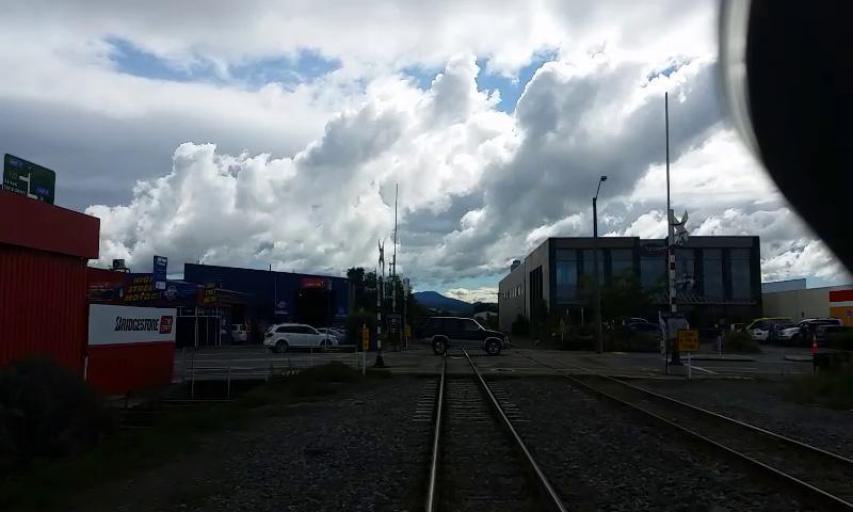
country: NZ
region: Canterbury
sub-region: Waimakariri District
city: Woodend
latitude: -43.3033
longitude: 172.5983
